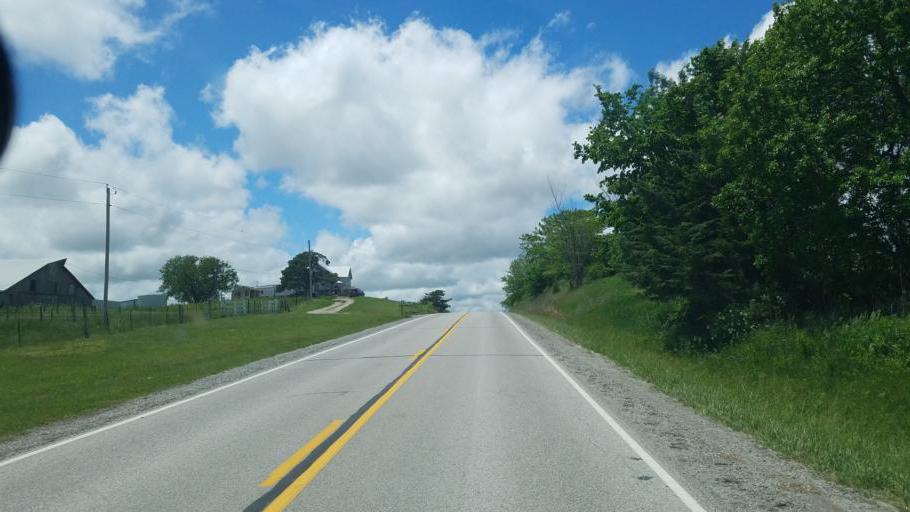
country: US
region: Iowa
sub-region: Decatur County
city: Lamoni
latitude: 40.6237
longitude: -93.8824
